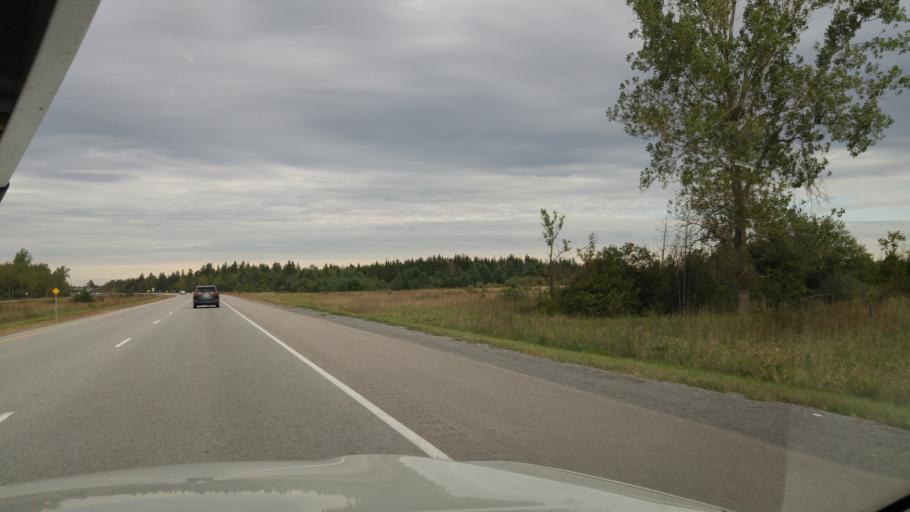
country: CA
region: Ontario
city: Bells Corners
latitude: 45.2899
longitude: -76.0109
